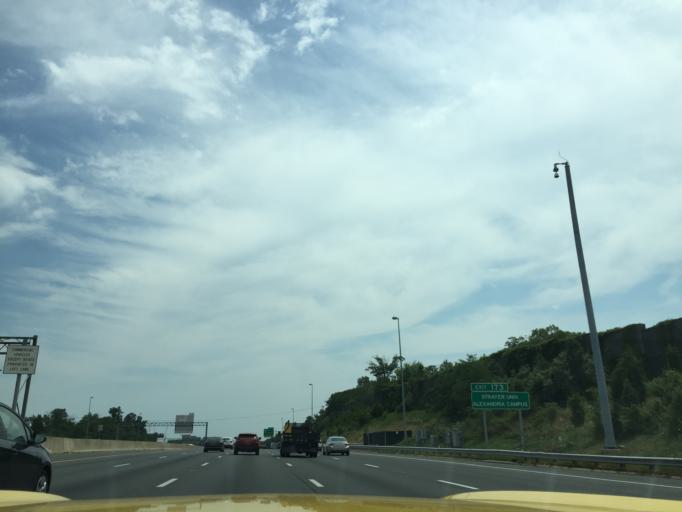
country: US
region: Virginia
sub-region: Fairfax County
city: Franconia
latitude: 38.7936
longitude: -77.1519
